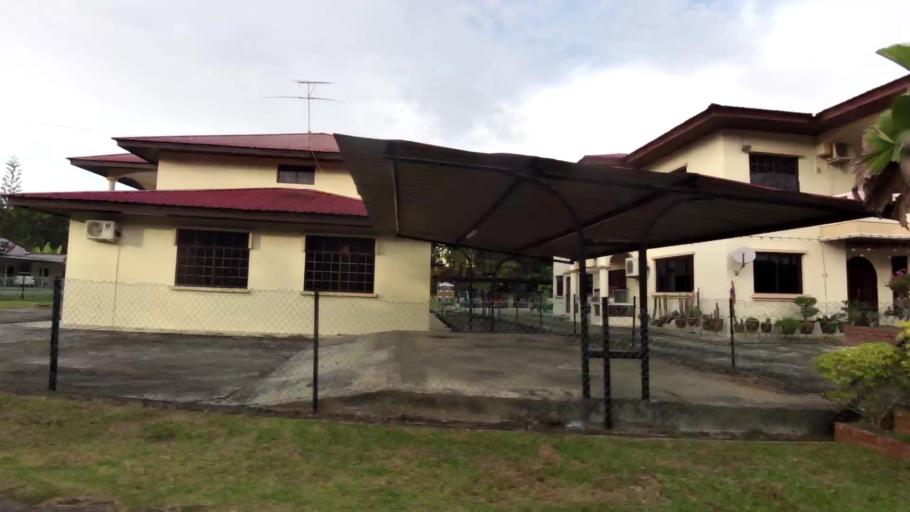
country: BN
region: Brunei and Muara
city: Bandar Seri Begawan
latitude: 4.9761
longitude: 114.9907
